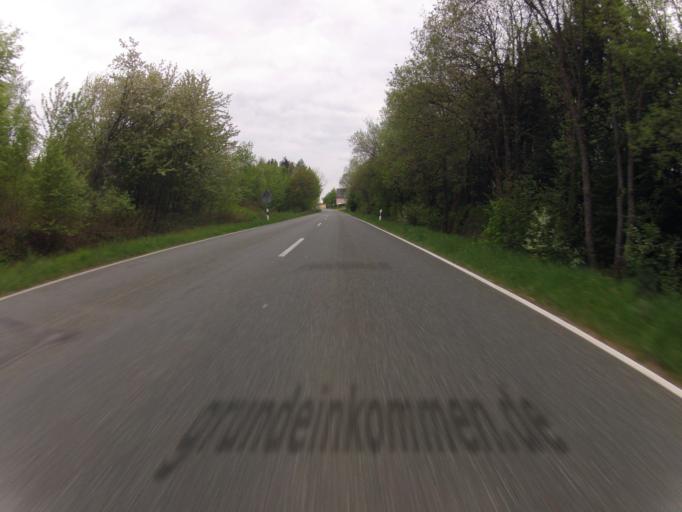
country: DE
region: Bavaria
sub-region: Upper Franconia
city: Zell im Fichtelgebirge
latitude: 50.1361
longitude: 11.8262
